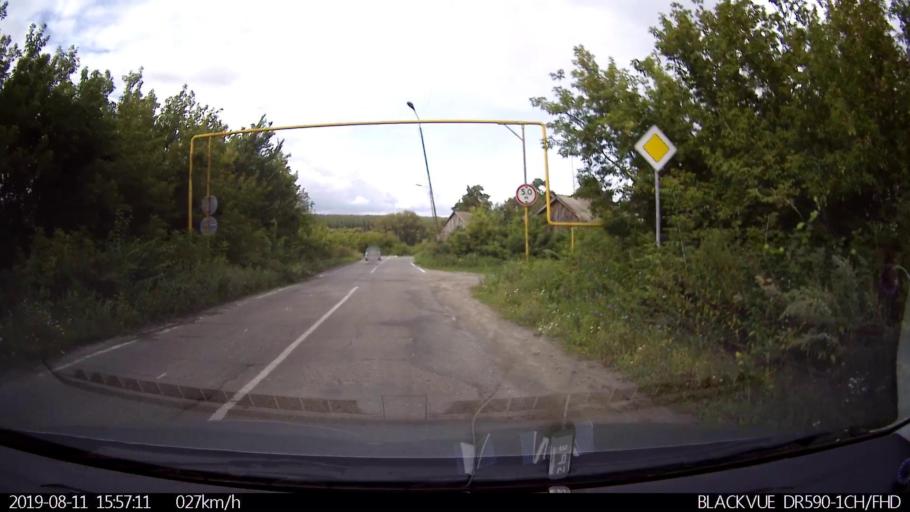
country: RU
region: Ulyanovsk
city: Ignatovka
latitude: 53.9500
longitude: 47.6526
